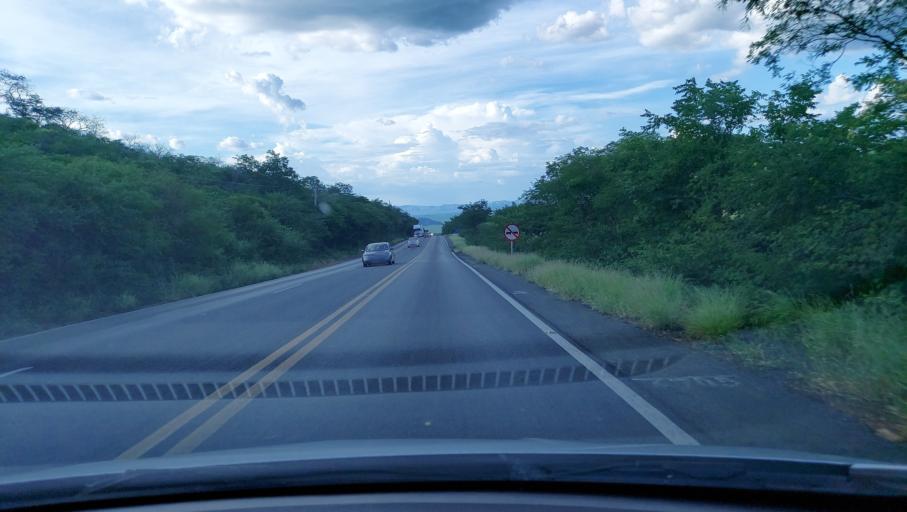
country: BR
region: Bahia
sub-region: Oliveira Dos Brejinhos
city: Beira Rio
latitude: -12.4079
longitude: -42.3740
